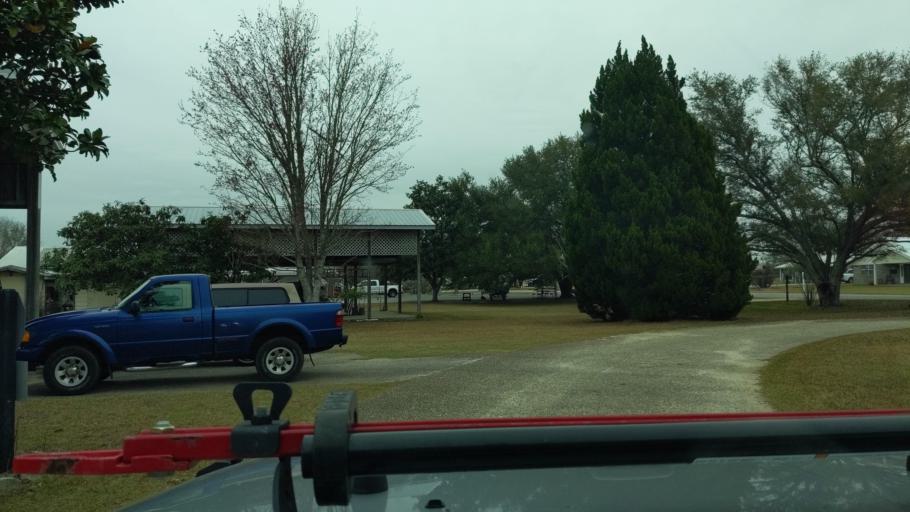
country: US
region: Alabama
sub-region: Baldwin County
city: Foley
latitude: 30.4594
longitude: -87.7795
